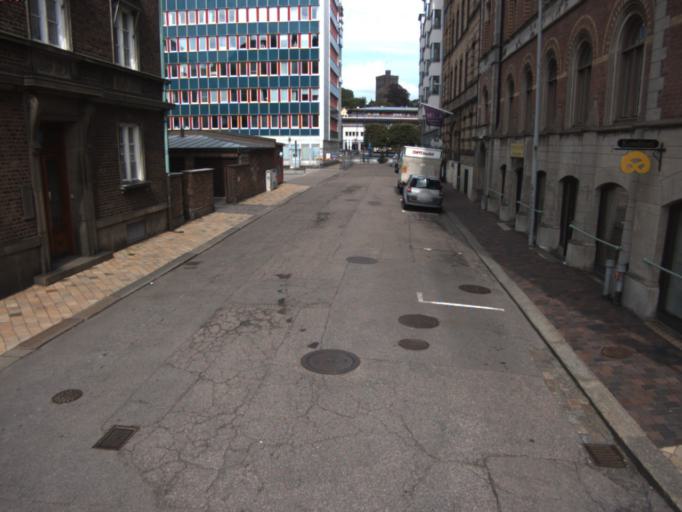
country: SE
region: Skane
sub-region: Helsingborg
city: Helsingborg
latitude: 56.0466
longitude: 12.6905
